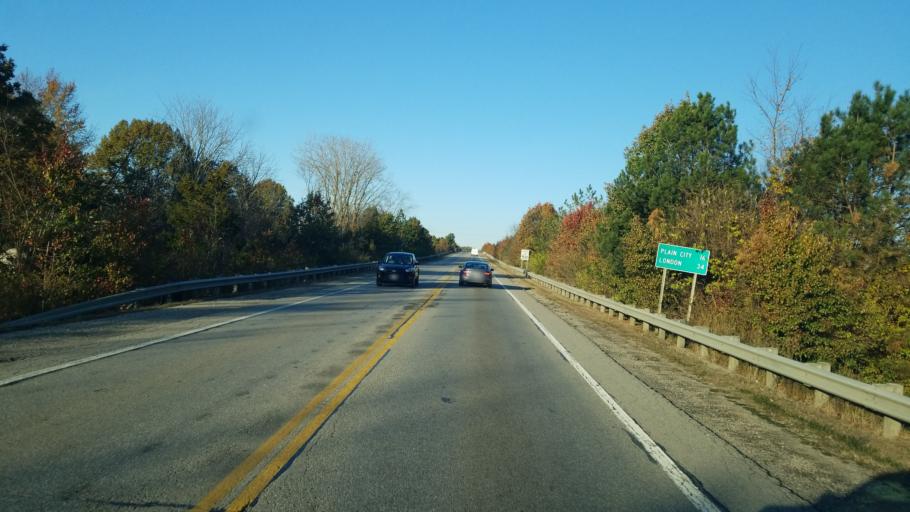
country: US
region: Ohio
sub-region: Delaware County
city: Delaware
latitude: 40.2767
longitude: -83.0769
